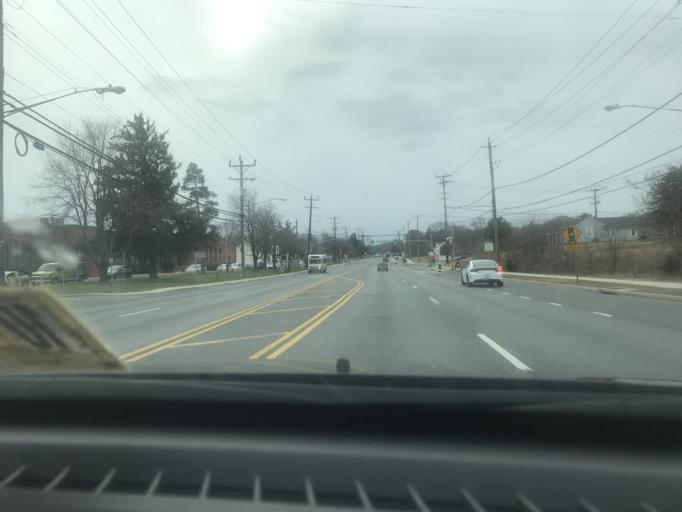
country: US
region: Maryland
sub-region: Prince George's County
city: Camp Springs
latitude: 38.8015
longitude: -76.9094
